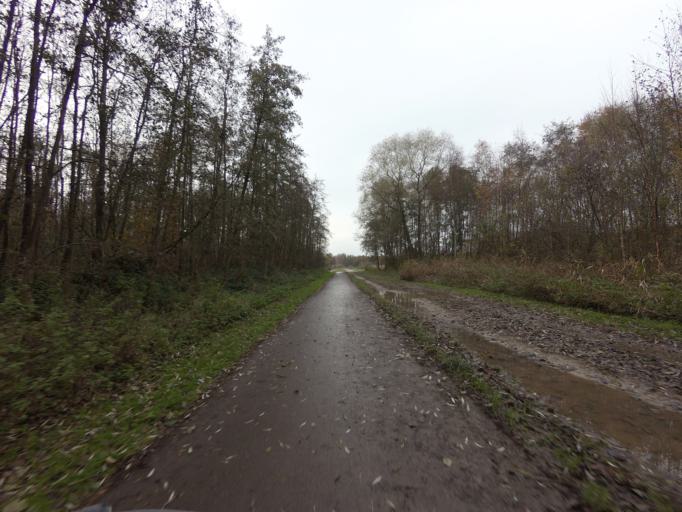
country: NL
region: North Holland
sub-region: Gemeente Amsterdam
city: Driemond
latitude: 52.3276
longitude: 4.9962
